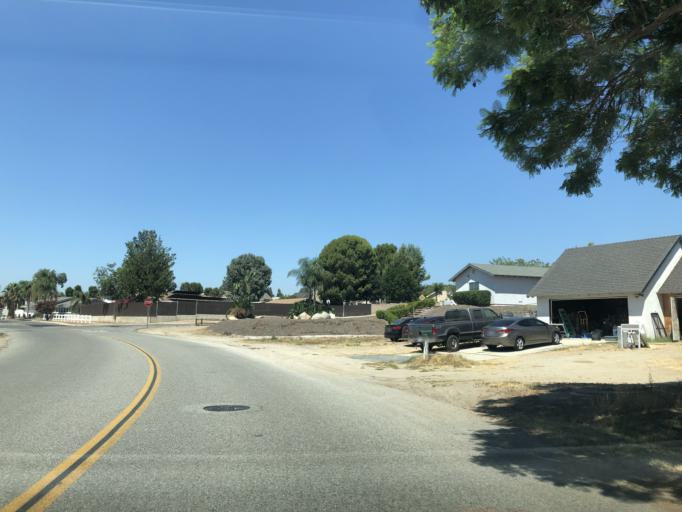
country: US
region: California
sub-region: Riverside County
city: Norco
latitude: 33.9127
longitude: -117.5799
